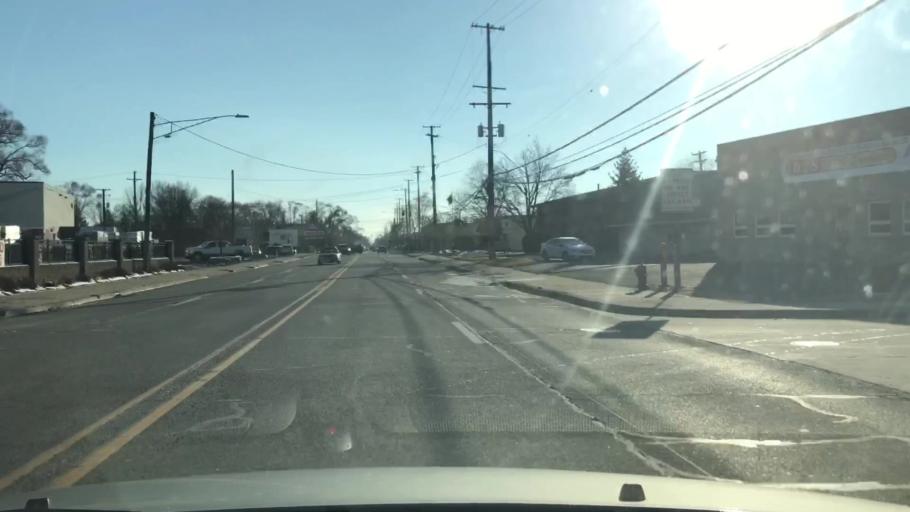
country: US
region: Michigan
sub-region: Oakland County
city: Clawson
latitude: 42.5410
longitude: -83.1341
